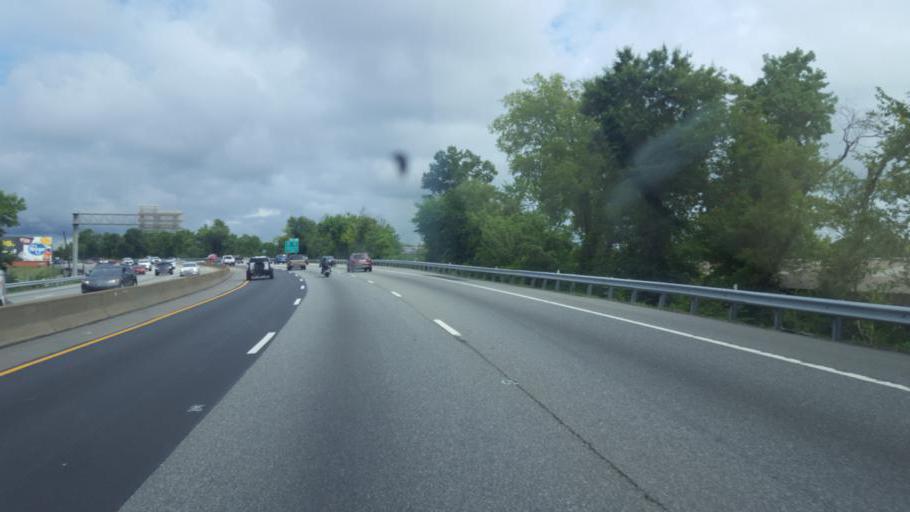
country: US
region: Virginia
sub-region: City of Richmond
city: Richmond
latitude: 37.5684
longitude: -77.4534
